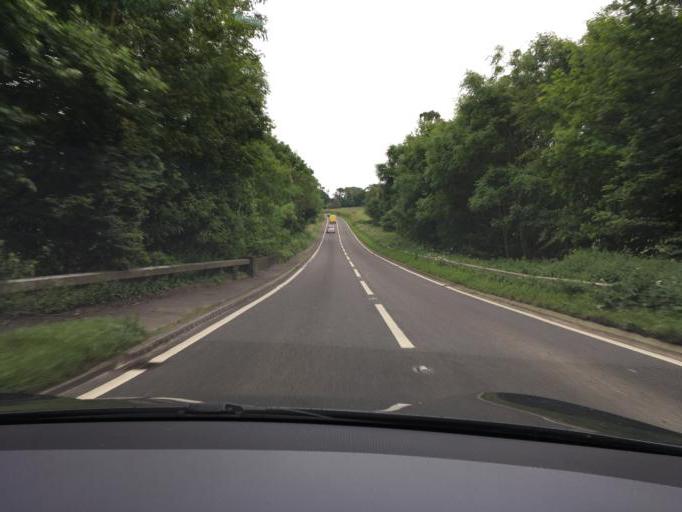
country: GB
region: England
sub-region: Derbyshire
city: Shirley
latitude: 52.9871
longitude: -1.6822
